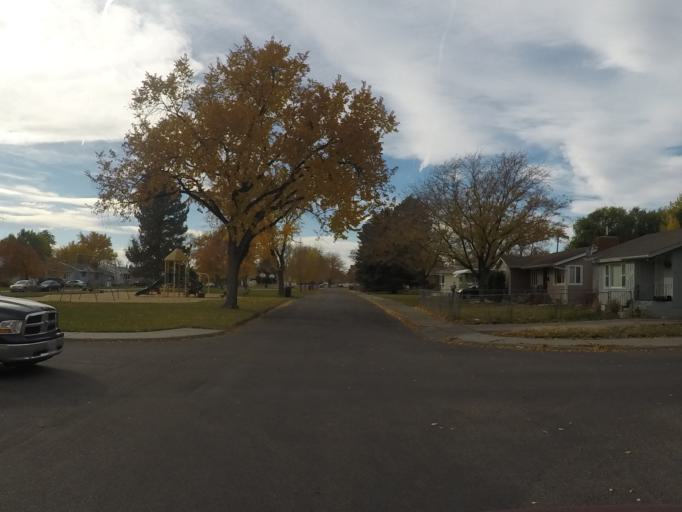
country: US
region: Montana
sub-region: Yellowstone County
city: Billings
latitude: 45.7873
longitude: -108.5510
